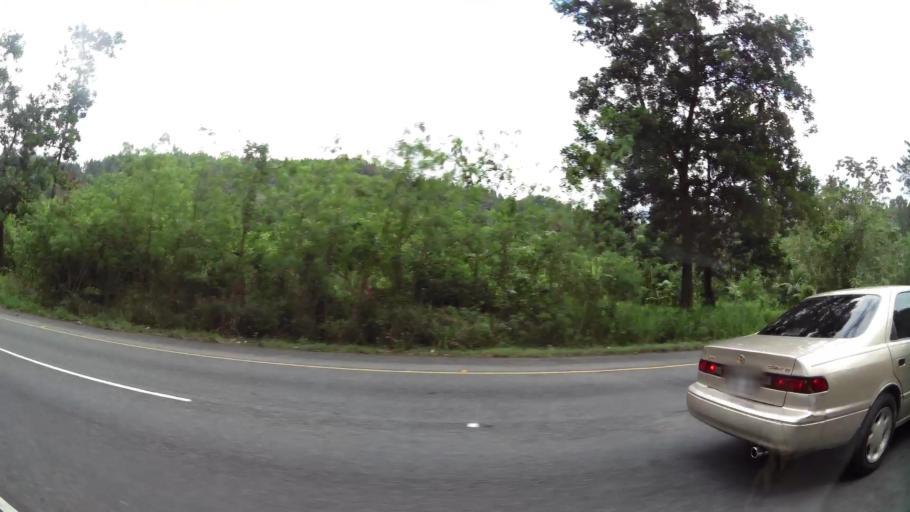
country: DO
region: Monsenor Nouel
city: Piedra Blanca
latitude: 18.8043
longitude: -70.2780
